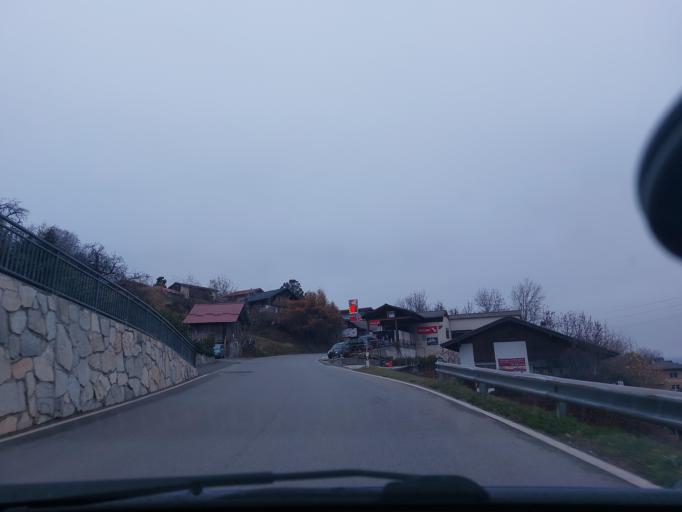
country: CH
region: Valais
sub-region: Conthey District
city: Basse-Nendaz
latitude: 46.1862
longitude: 7.3041
